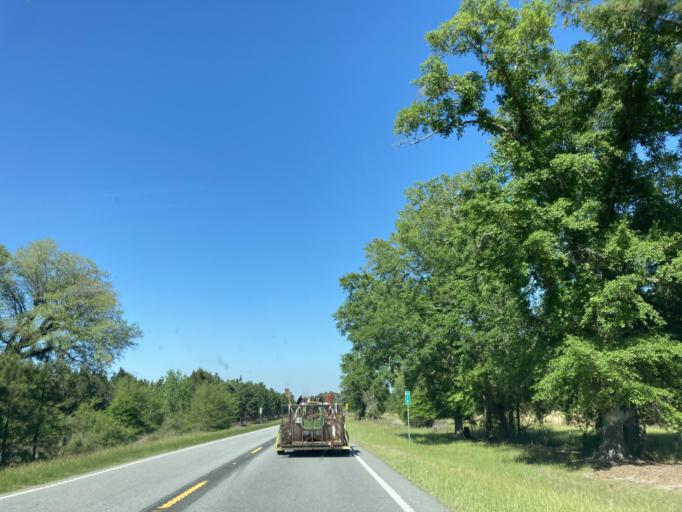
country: US
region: Georgia
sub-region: Baker County
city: Newton
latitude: 31.3436
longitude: -84.3090
